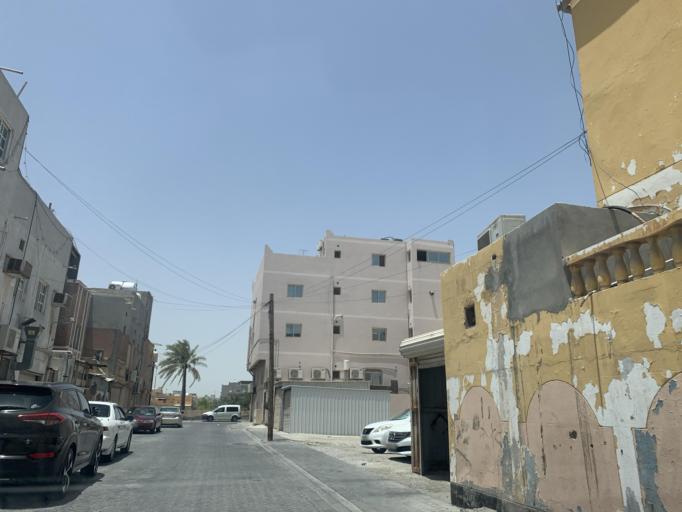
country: BH
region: Northern
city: Sitrah
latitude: 26.1581
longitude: 50.6235
